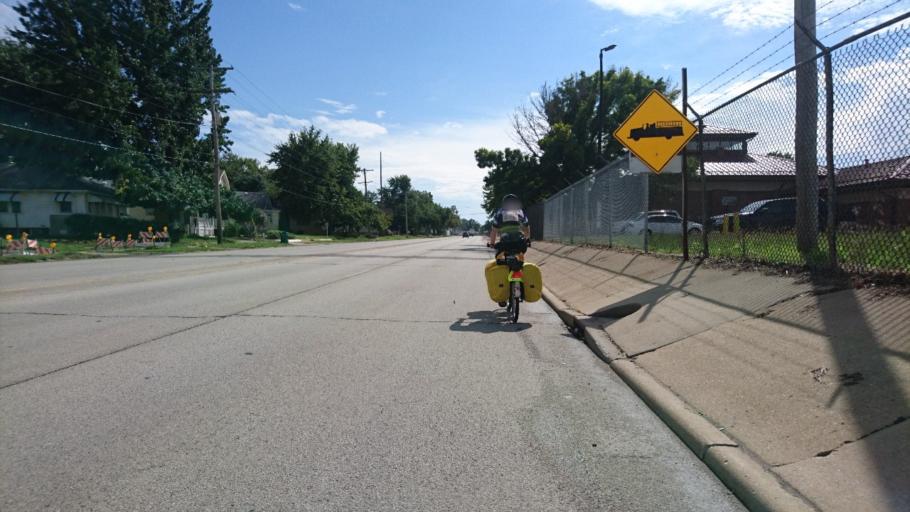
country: US
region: Illinois
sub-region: Sangamon County
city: Grandview
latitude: 39.8357
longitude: -89.6353
